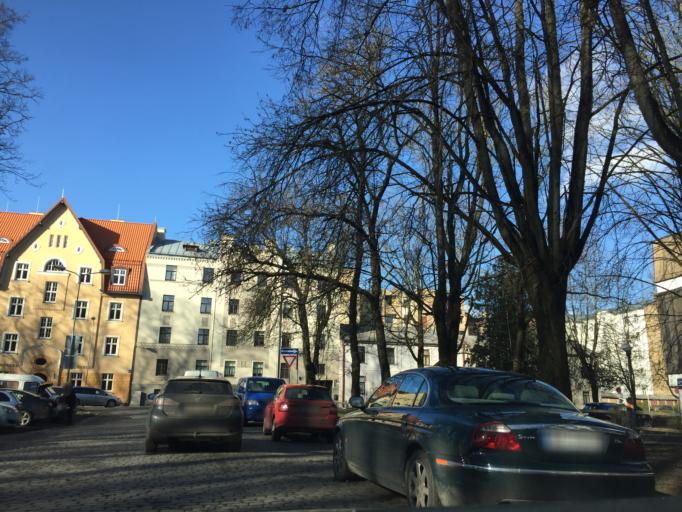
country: LV
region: Riga
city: Riga
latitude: 56.9745
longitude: 24.1455
